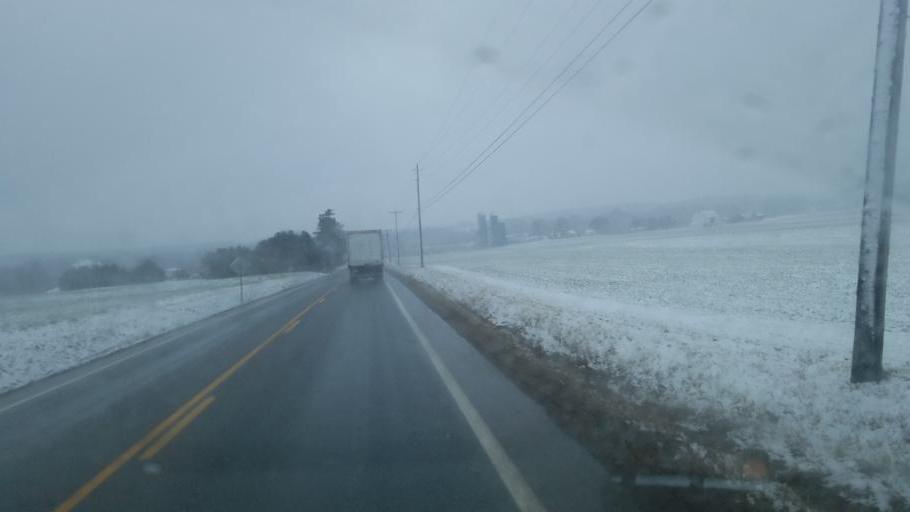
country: US
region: Ohio
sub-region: Portage County
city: Garrettsville
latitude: 41.3573
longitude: -81.0799
